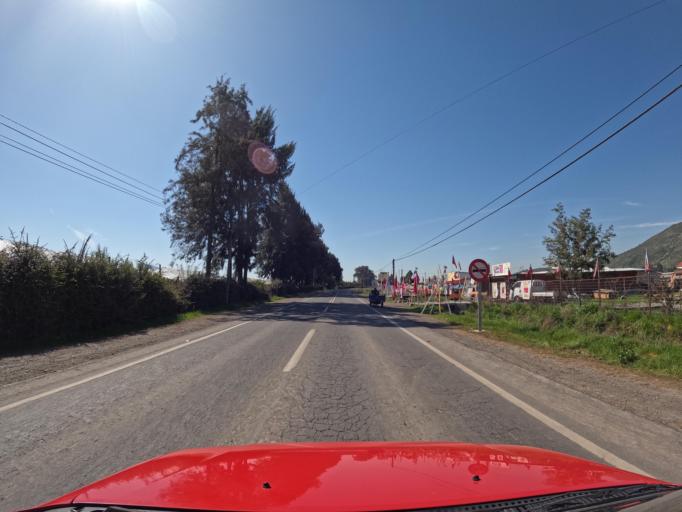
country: CL
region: Maule
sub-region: Provincia de Curico
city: Rauco
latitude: -35.0083
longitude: -71.4111
